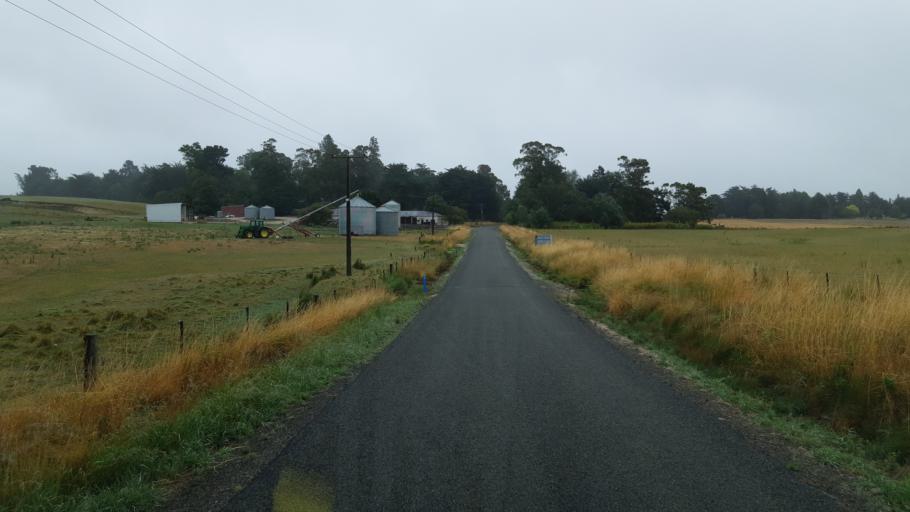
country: NZ
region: Otago
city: Oamaru
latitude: -44.9429
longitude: 170.6311
